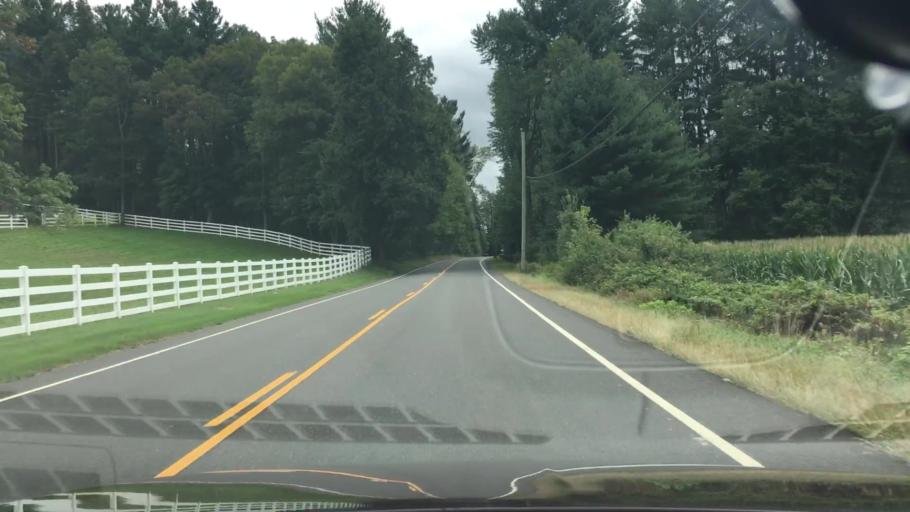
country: US
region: Connecticut
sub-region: Tolland County
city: Somers
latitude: 42.0273
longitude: -72.4533
